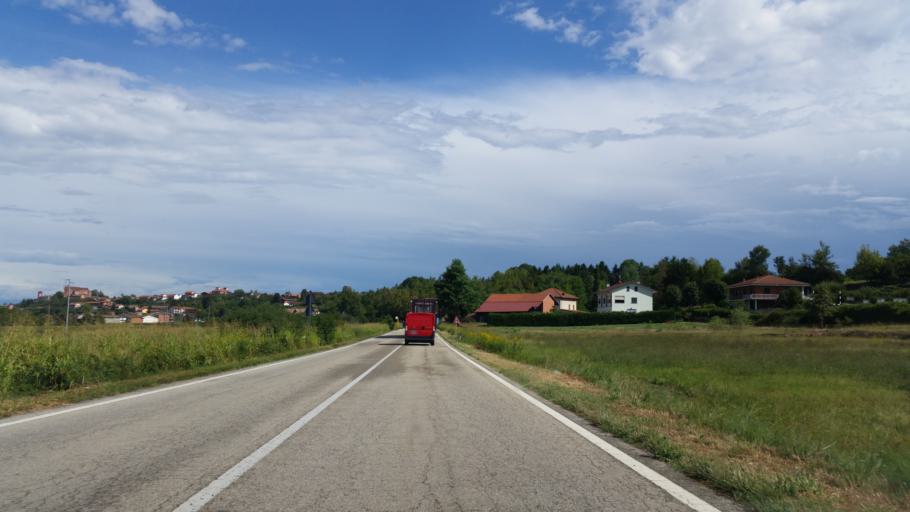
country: IT
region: Piedmont
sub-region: Provincia di Torino
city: Pralormo
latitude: 44.8488
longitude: 7.9087
